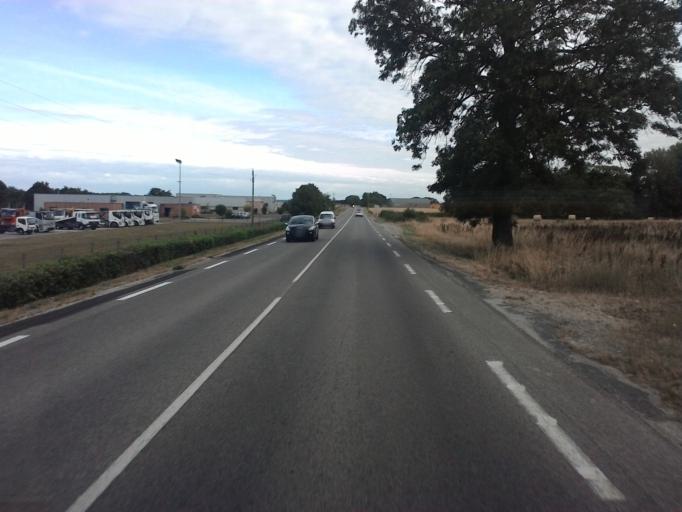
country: FR
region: Rhone-Alpes
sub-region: Departement de l'Ain
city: Saint-Martin-du-Mont
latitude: 46.0908
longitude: 5.3145
